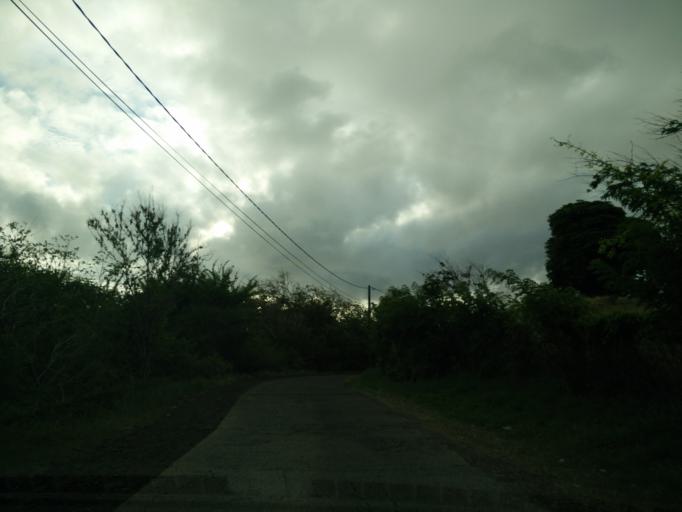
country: MQ
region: Martinique
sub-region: Martinique
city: Le Marin
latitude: 14.4380
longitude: -60.8329
